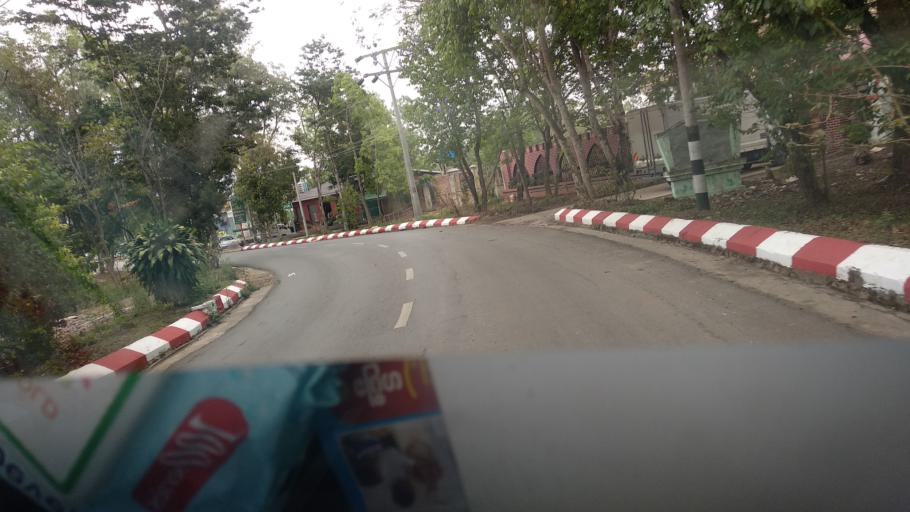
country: MM
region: Mandalay
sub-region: Pyin Oo Lwin District
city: Pyin Oo Lwin
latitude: 22.0143
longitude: 96.4611
